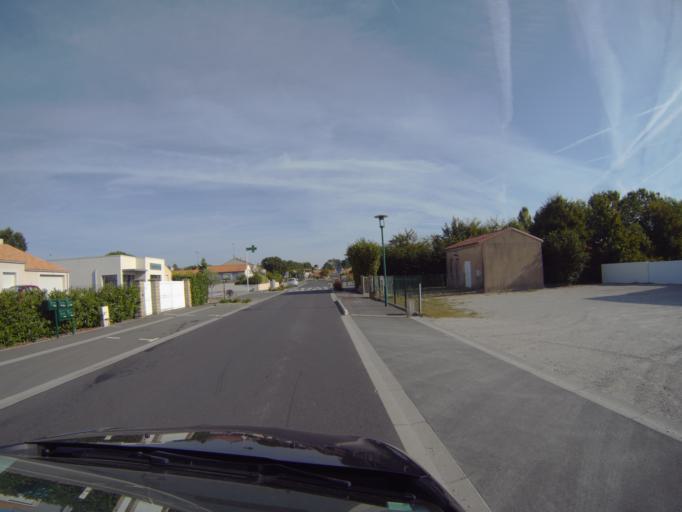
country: FR
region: Pays de la Loire
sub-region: Departement de la Vendee
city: Les Clouzeaux
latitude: 46.6325
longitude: -1.5096
